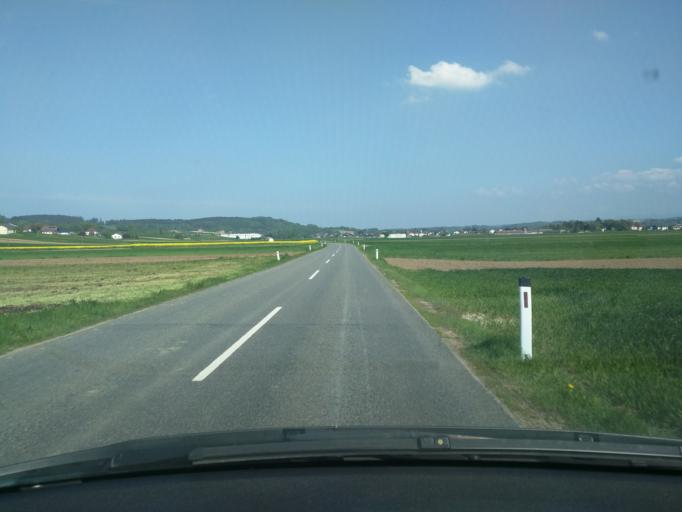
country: AT
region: Lower Austria
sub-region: Politischer Bezirk Amstetten
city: Sankt Georgen am Ybbsfelde
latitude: 48.1302
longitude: 14.9639
